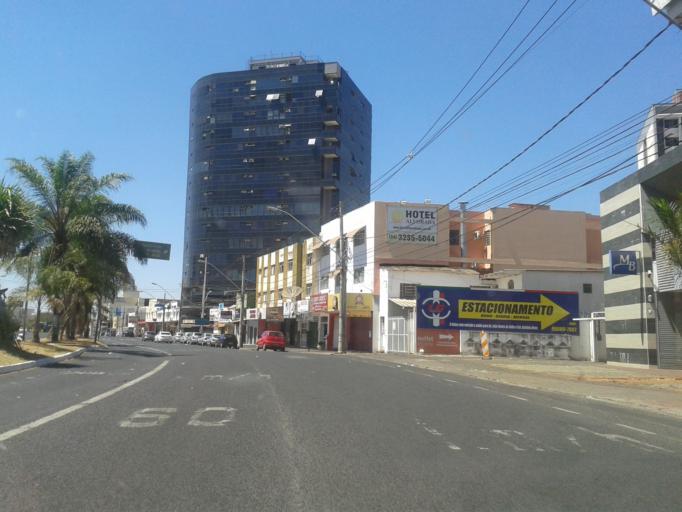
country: BR
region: Minas Gerais
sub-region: Uberlandia
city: Uberlandia
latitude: -18.9165
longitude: -48.2738
